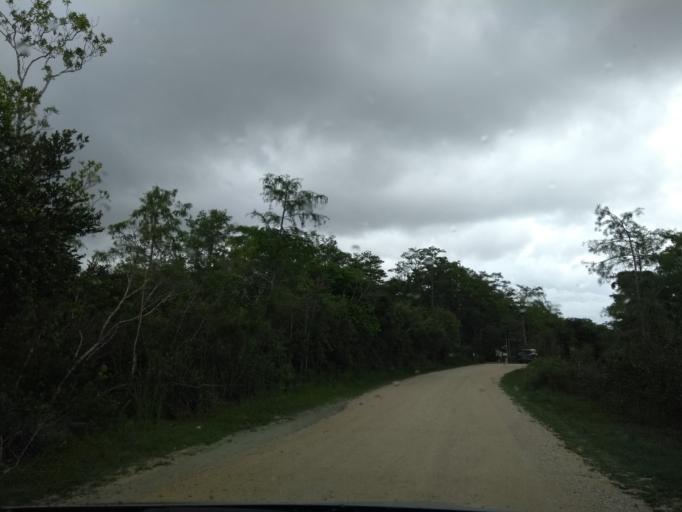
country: US
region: Florida
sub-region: Miami-Dade County
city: The Hammocks
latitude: 25.7466
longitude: -80.9534
